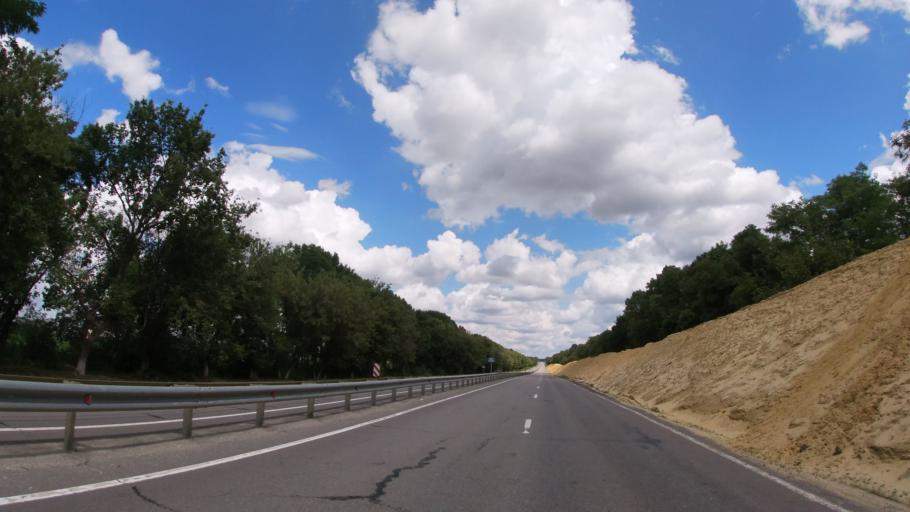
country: RU
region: Belgorod
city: Mayskiy
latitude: 50.4208
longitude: 36.3777
